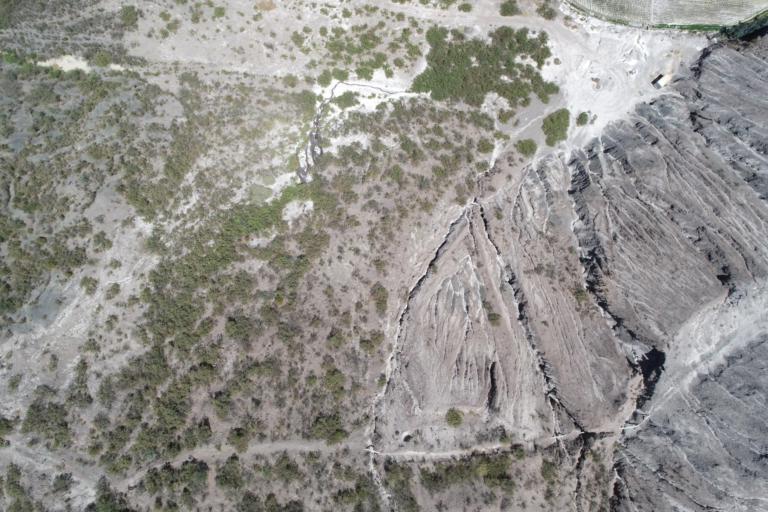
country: BO
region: La Paz
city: La Paz
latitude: -16.6128
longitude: -68.0629
